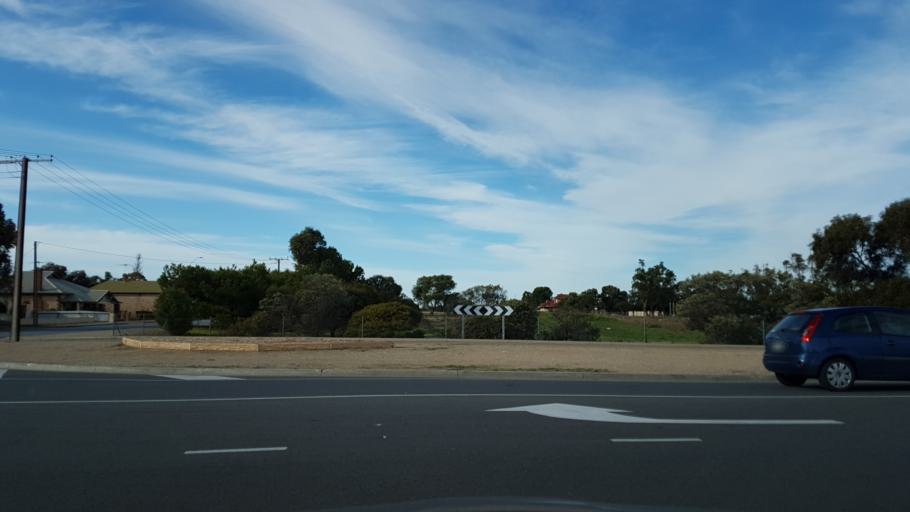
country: AU
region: South Australia
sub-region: Murray Bridge
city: Tailem Bend
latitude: -35.2522
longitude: 139.4543
